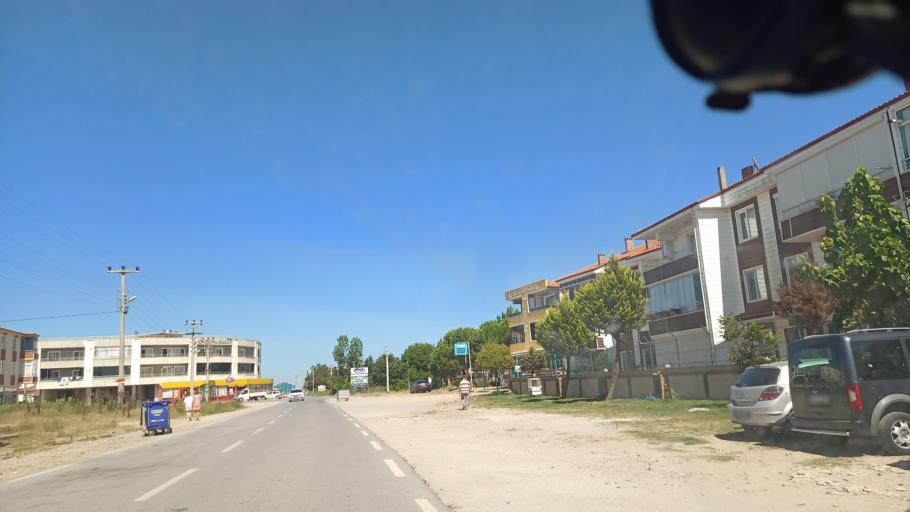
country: TR
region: Sakarya
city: Karasu
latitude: 41.1193
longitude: 30.6536
